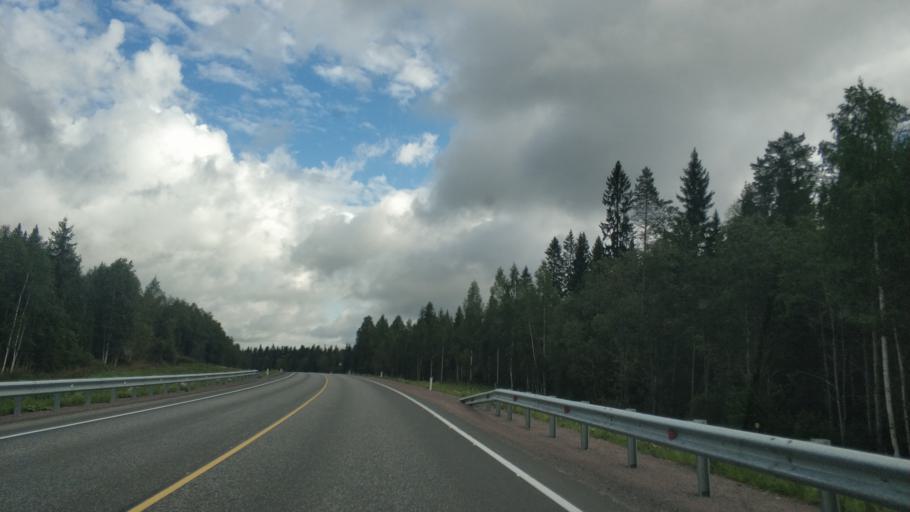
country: RU
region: Republic of Karelia
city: Ruskeala
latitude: 61.8634
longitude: 30.6533
